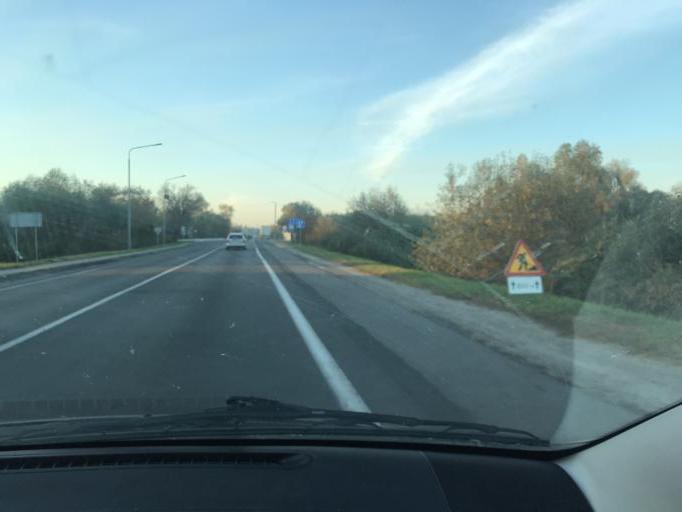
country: BY
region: Brest
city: Pinsk
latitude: 52.1029
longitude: 26.1124
